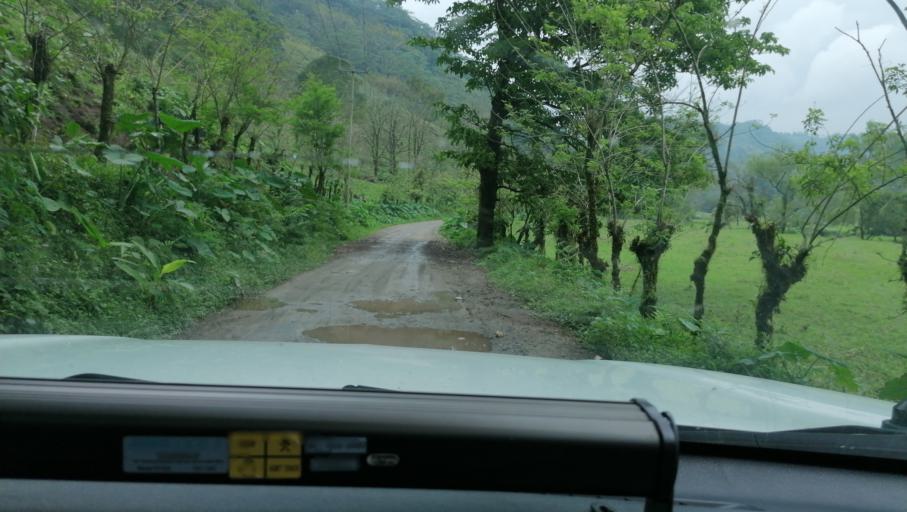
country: MX
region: Chiapas
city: Ixtacomitan
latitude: 17.3572
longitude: -93.1671
